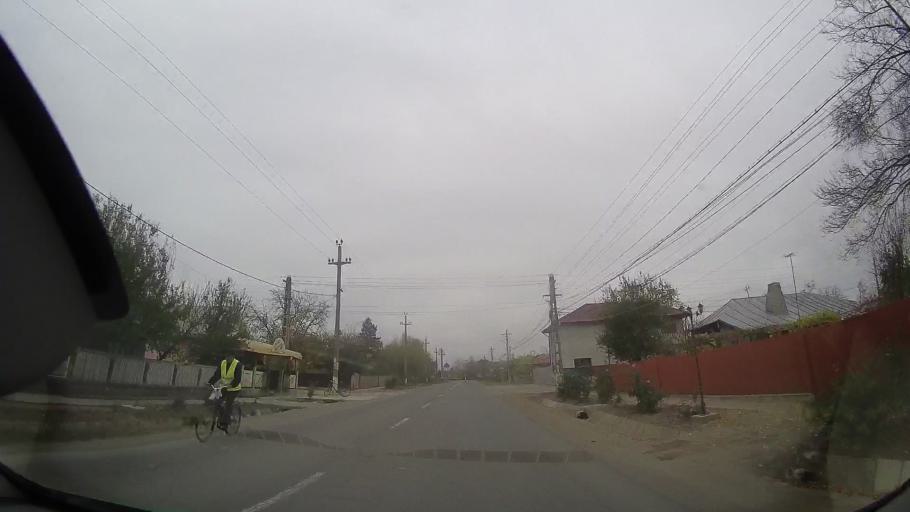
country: RO
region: Ialomita
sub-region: Comuna Grivita
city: Grivita
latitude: 44.7345
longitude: 27.2935
